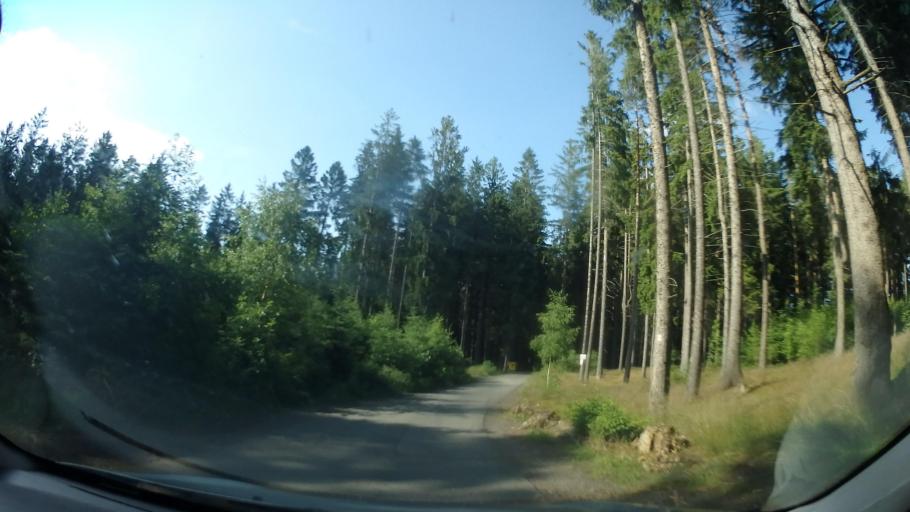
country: CZ
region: Vysocina
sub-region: Okres Zd'ar nad Sazavou
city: Svratka
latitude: 49.7280
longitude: 16.0449
